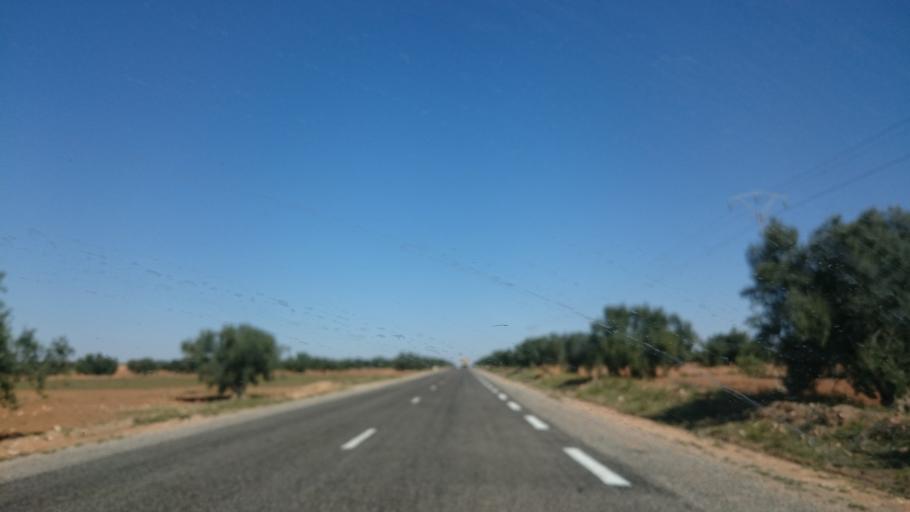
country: TN
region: Safaqis
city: Sfax
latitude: 34.8456
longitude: 10.4521
